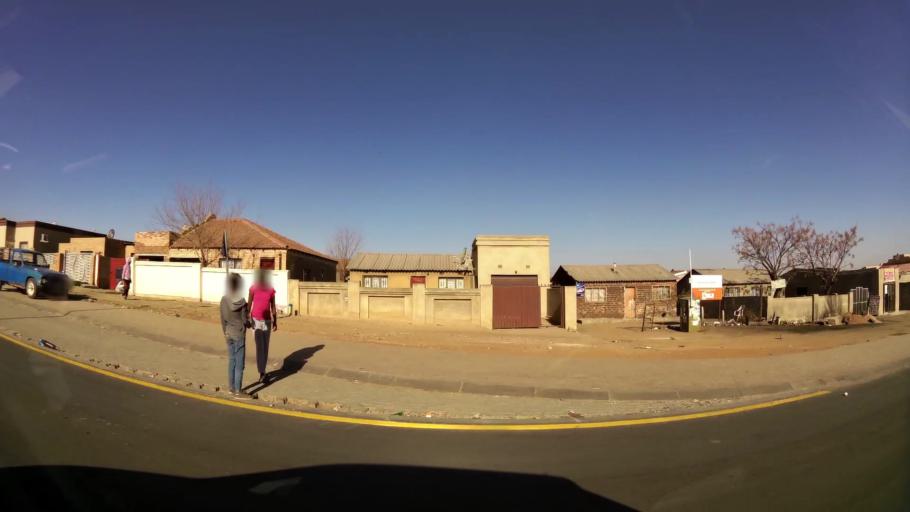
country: ZA
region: Gauteng
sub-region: Ekurhuleni Metropolitan Municipality
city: Tembisa
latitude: -26.0253
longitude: 28.2194
